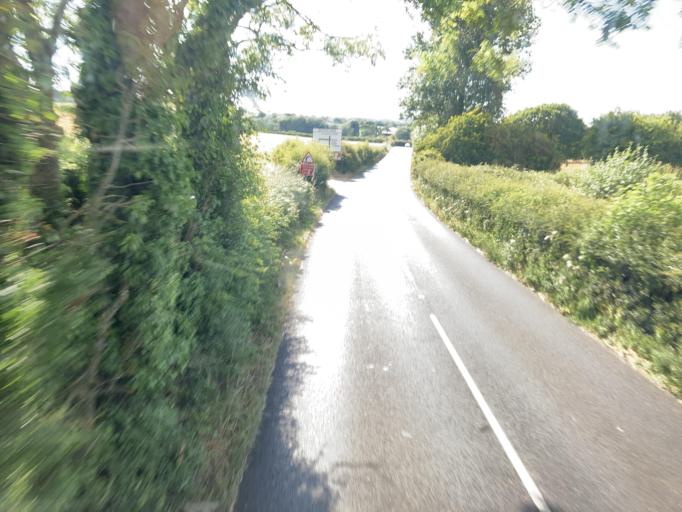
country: GB
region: England
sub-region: Isle of Wight
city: Newchurch
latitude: 50.6305
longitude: -1.2185
